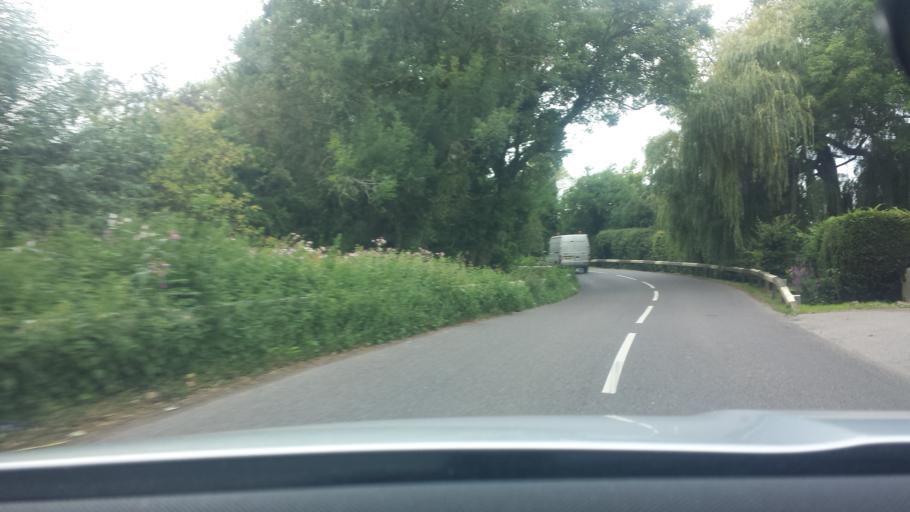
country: GB
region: England
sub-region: Kent
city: Marden
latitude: 51.1835
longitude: 0.4835
